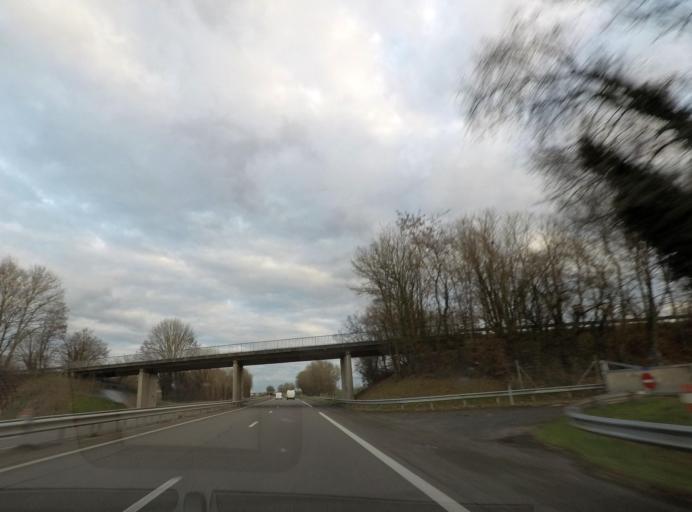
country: FR
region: Rhone-Alpes
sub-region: Departement de l'Ain
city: Saint-Cyr-sur-Menthon
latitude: 46.2840
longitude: 4.9506
